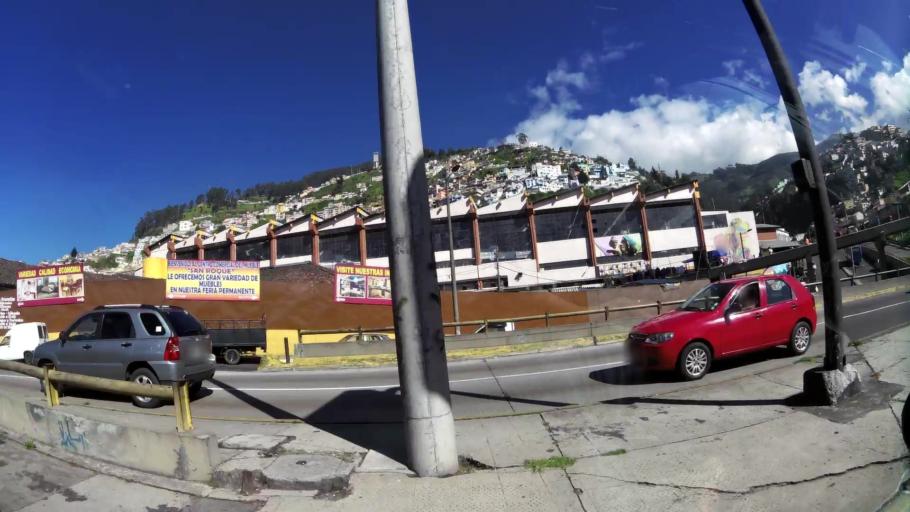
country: EC
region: Pichincha
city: Quito
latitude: -0.2196
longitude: -78.5206
